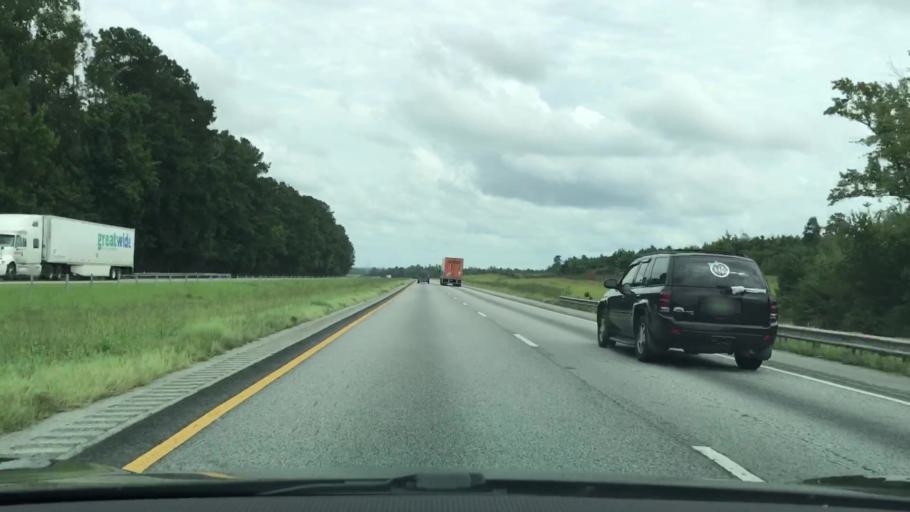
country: US
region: Alabama
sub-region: Lee County
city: Opelika
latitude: 32.6837
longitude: -85.3233
